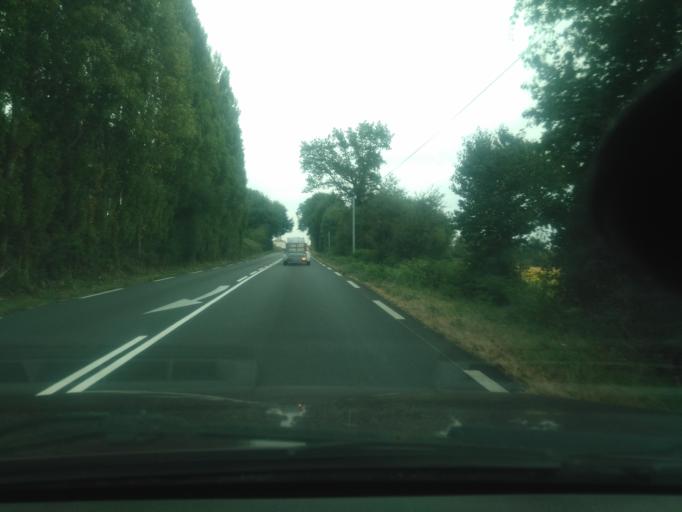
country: FR
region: Pays de la Loire
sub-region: Departement de la Vendee
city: Bazoges-en-Pareds
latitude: 46.6769
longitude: -0.8903
